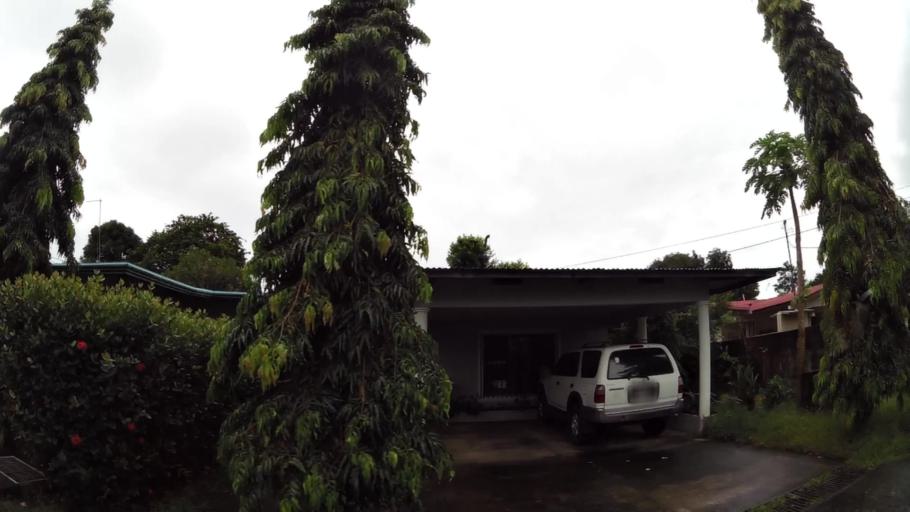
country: PA
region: Chiriqui
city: David
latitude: 8.4240
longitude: -82.4497
